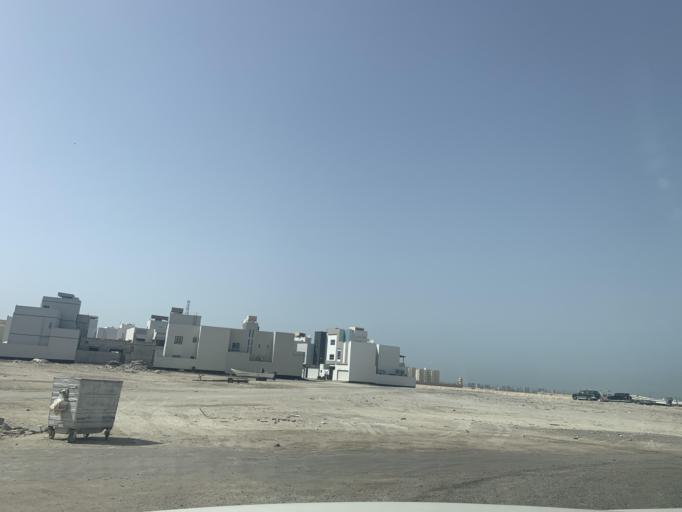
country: BH
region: Northern
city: Sitrah
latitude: 26.1700
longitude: 50.6283
